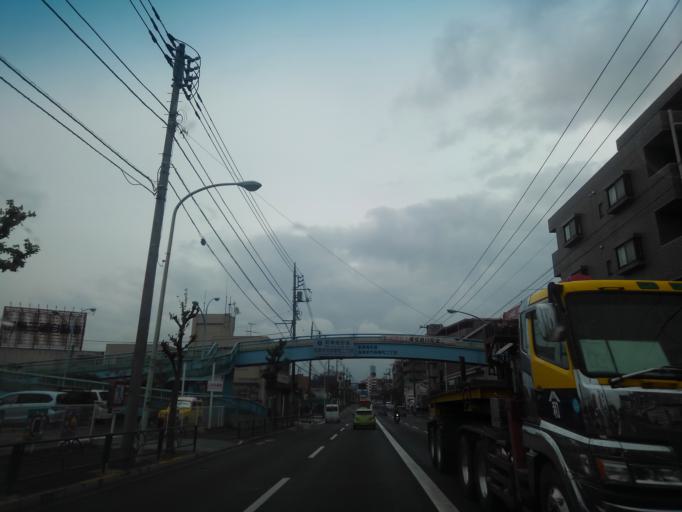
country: JP
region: Tokyo
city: Tanashicho
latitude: 35.7332
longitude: 139.5335
